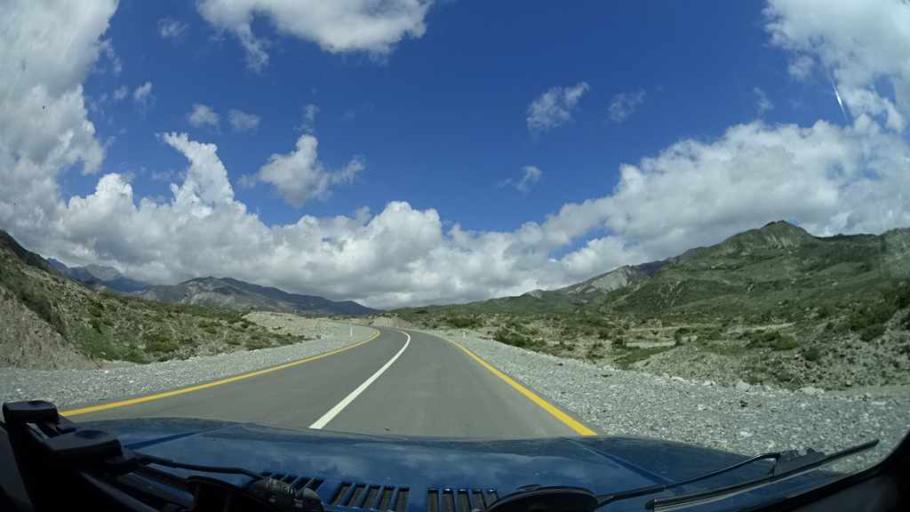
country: AZ
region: Ismayilli
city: Basqal
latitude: 40.8621
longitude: 48.4013
